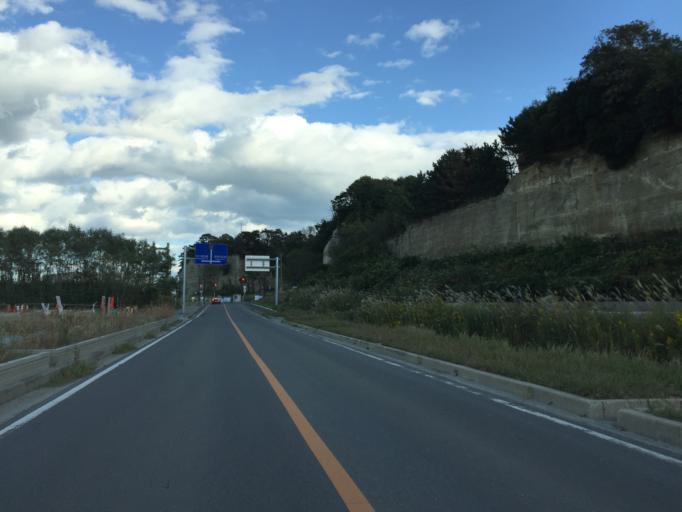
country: JP
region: Miyagi
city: Marumori
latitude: 37.8267
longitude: 140.9690
